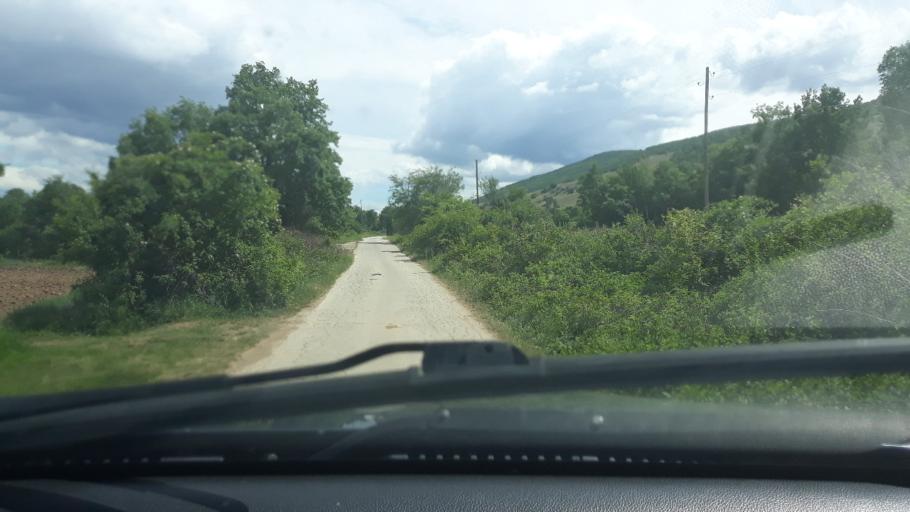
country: MK
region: Krivogastani
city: Krivogashtani
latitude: 41.3276
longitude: 21.3033
